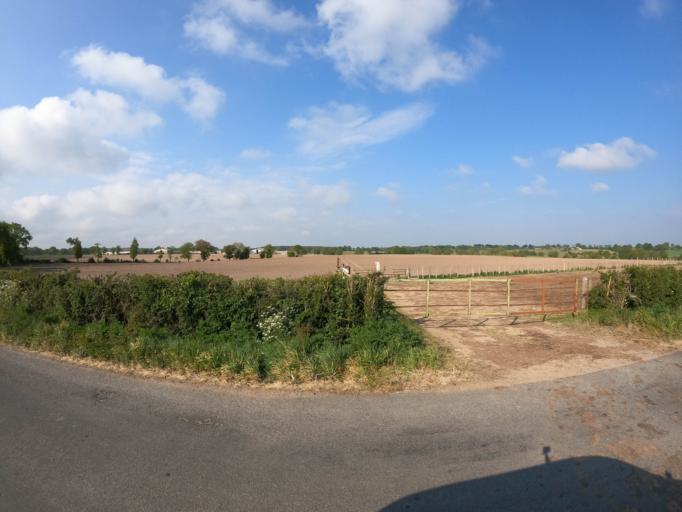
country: FR
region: Pays de la Loire
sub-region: Departement de Maine-et-Loire
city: Roussay
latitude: 47.0694
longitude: -1.0467
